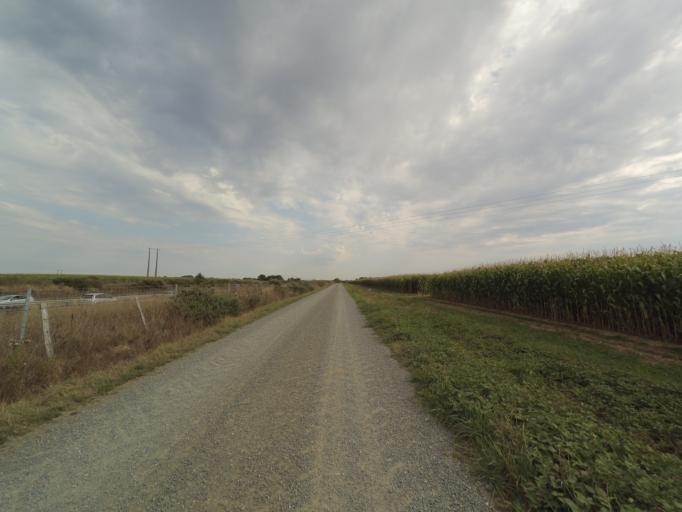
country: FR
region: Pays de la Loire
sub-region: Departement de la Vendee
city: Bouffere
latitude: 46.9764
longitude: -1.3715
